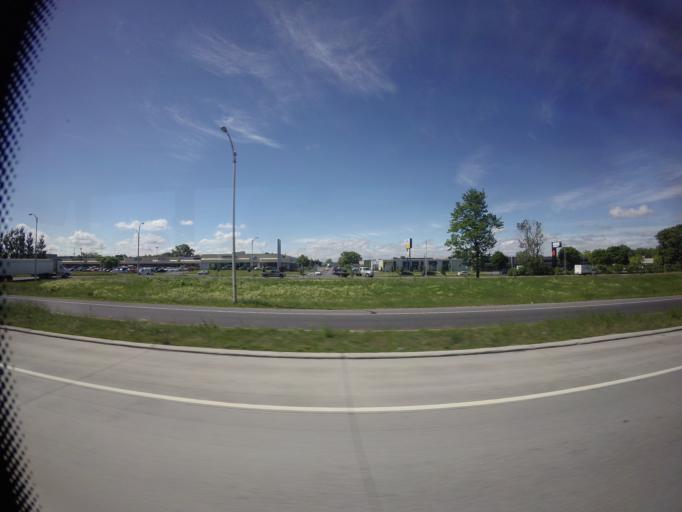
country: CA
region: Quebec
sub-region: Monteregie
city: Boucherville
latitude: 45.5754
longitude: -73.4616
